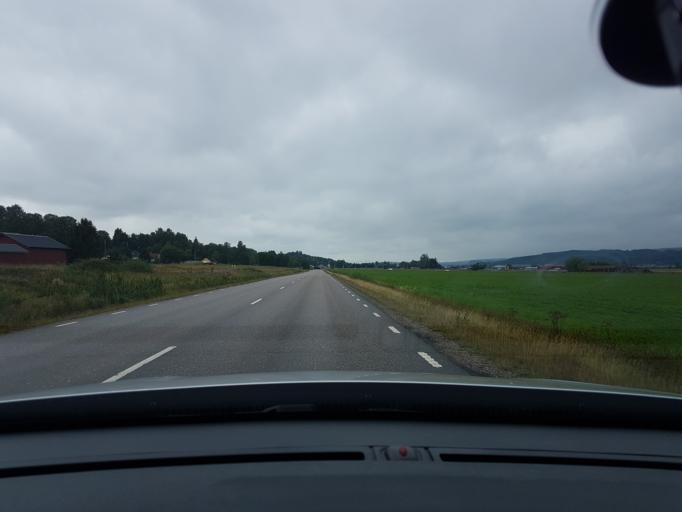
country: SE
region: Vaestra Goetaland
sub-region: Ale Kommun
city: Alvangen
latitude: 57.9695
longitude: 12.1599
